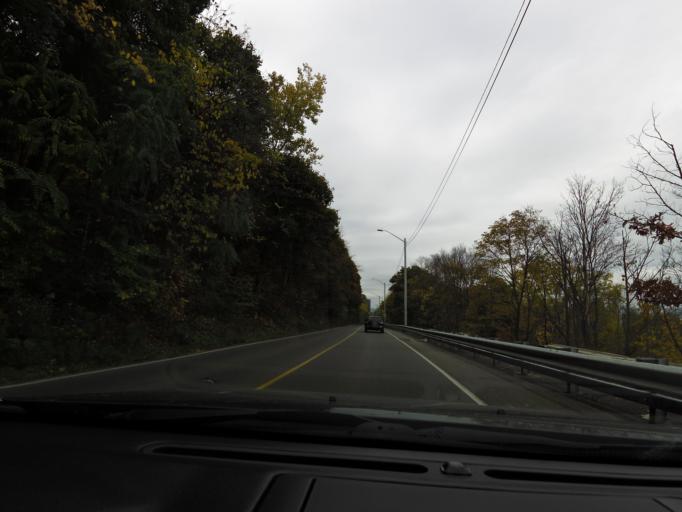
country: CA
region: Ontario
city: Hamilton
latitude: 43.2446
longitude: -79.8550
